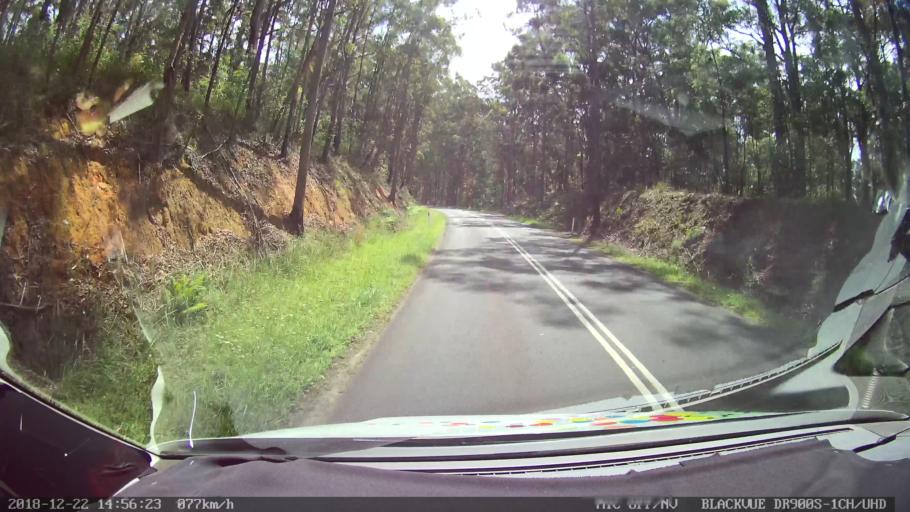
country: AU
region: New South Wales
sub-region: Bellingen
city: Dorrigo
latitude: -30.2325
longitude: 152.5132
